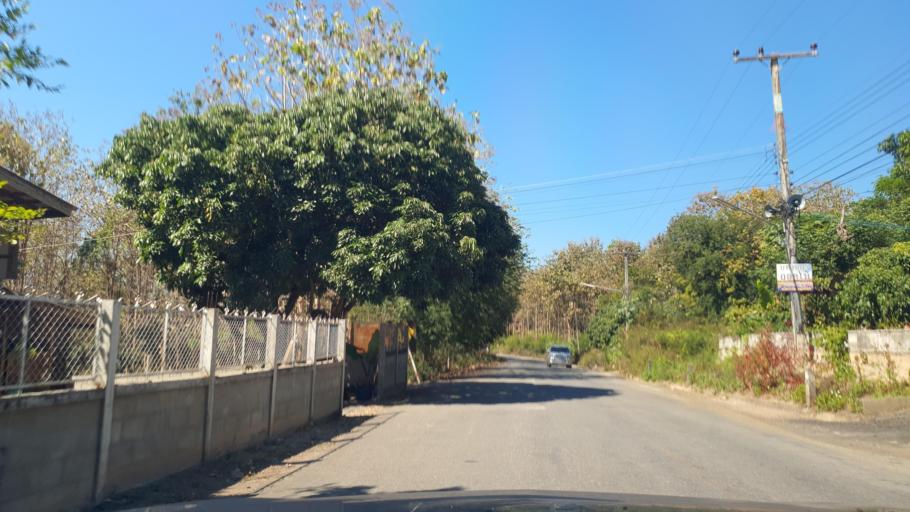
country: TH
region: Chiang Mai
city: Mae Wang
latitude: 18.6802
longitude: 98.8181
